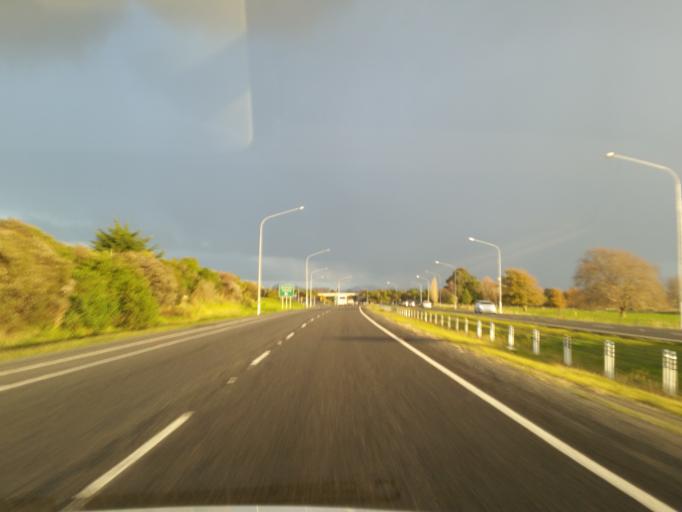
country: NZ
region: Waikato
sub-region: Waikato District
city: Te Kauwhata
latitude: -37.4841
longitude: 175.1605
